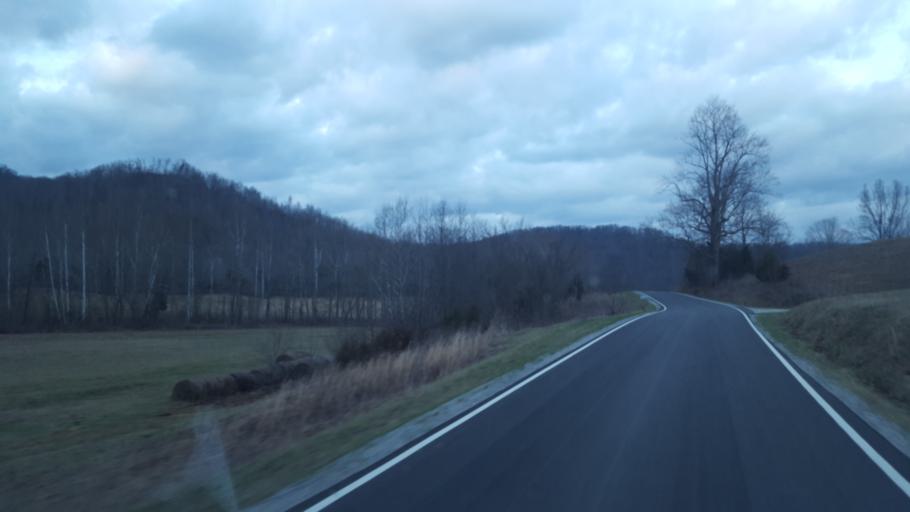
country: US
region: Kentucky
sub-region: Lewis County
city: Vanceburg
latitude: 38.5417
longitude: -83.4648
